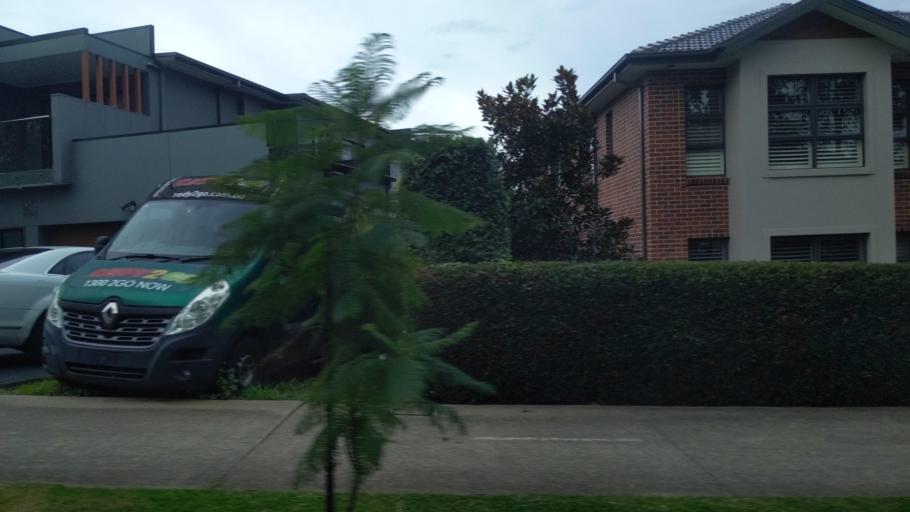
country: AU
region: New South Wales
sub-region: Blacktown
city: Quakers Hill
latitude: -33.7263
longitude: 150.8629
